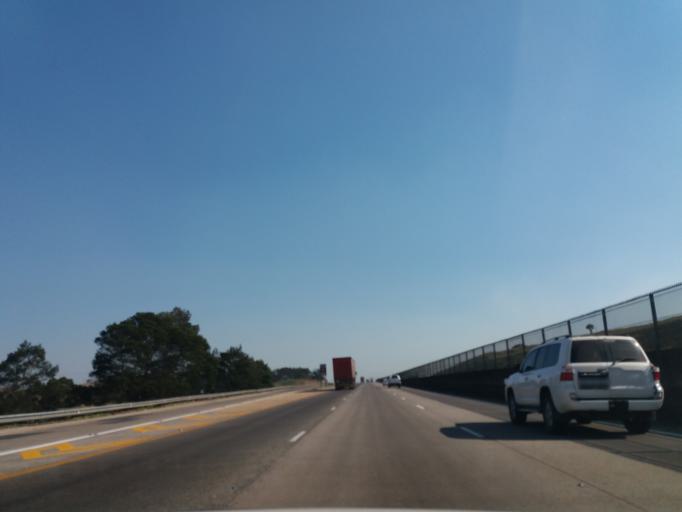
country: ZA
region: KwaZulu-Natal
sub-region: eThekwini Metropolitan Municipality
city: Mpumalanga
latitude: -29.7388
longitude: 30.6393
